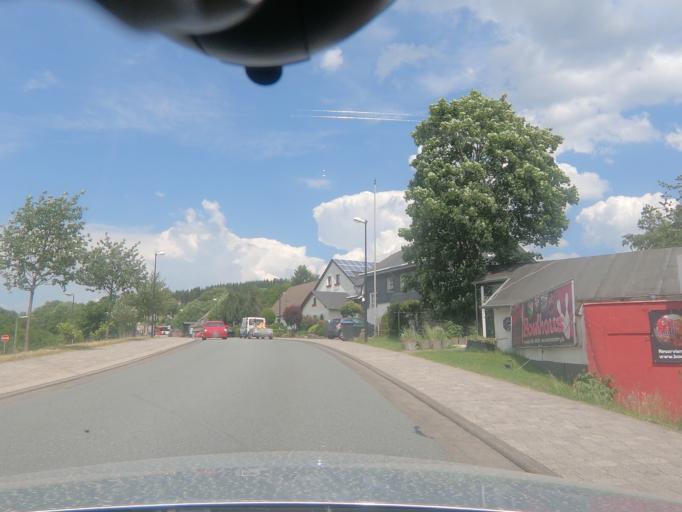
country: DE
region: North Rhine-Westphalia
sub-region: Regierungsbezirk Arnsberg
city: Winterberg
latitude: 51.2003
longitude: 8.5335
